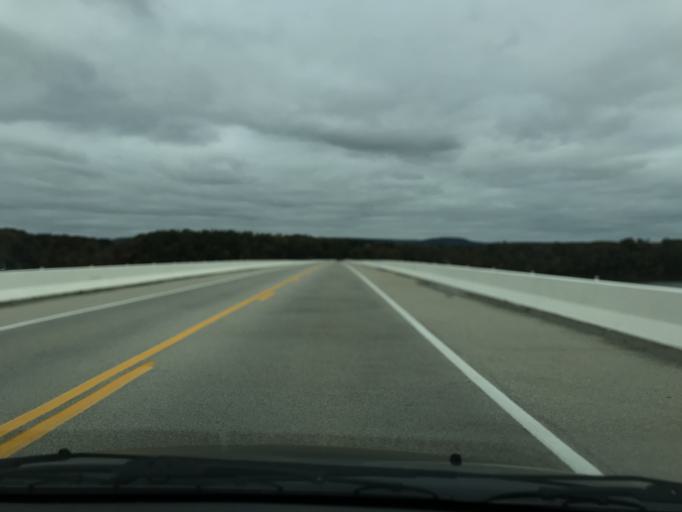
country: US
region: Tennessee
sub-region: Rhea County
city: Graysville
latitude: 35.4083
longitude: -85.0181
